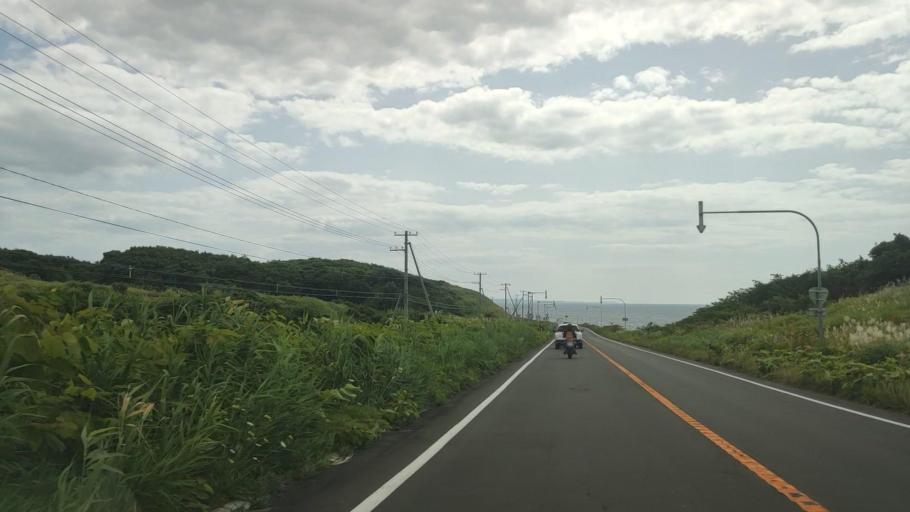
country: JP
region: Hokkaido
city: Rumoi
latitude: 44.5112
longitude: 141.7657
